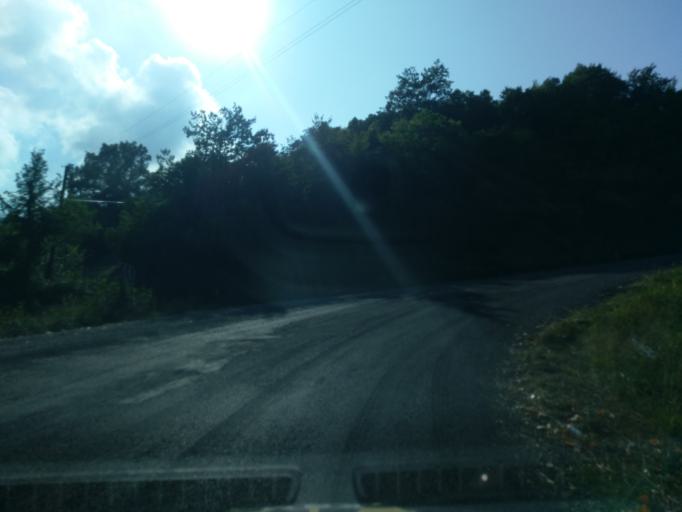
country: TR
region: Sinop
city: Ayancik
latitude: 41.9413
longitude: 34.6779
